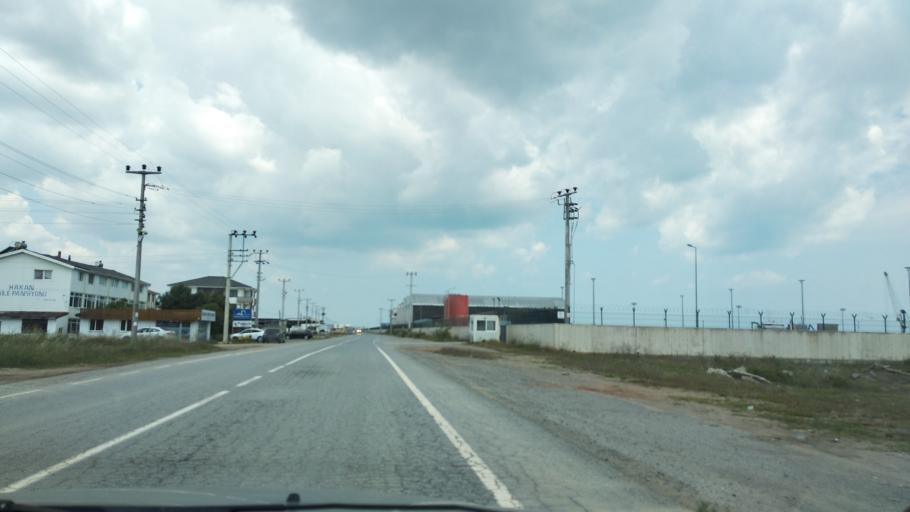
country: TR
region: Sakarya
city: Karasu
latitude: 41.1162
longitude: 30.6765
